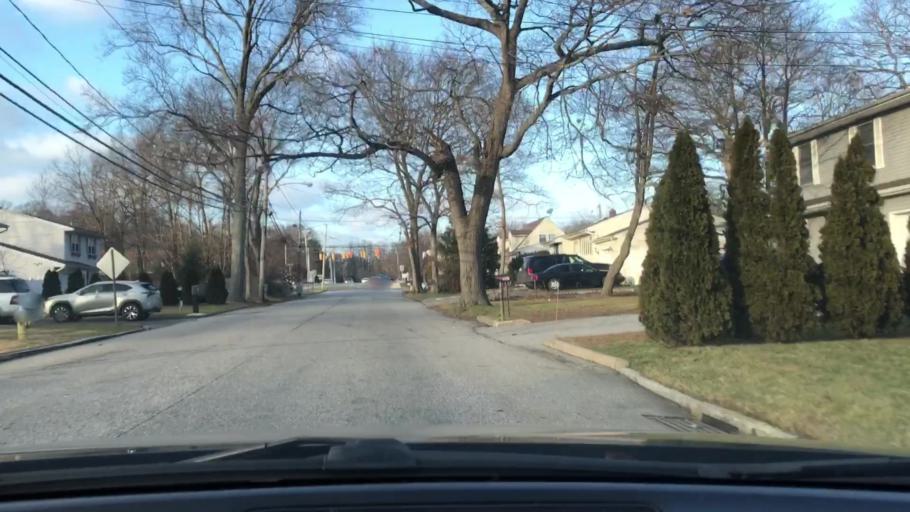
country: US
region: New York
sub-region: Suffolk County
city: Holbrook
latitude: 40.8301
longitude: -73.0862
